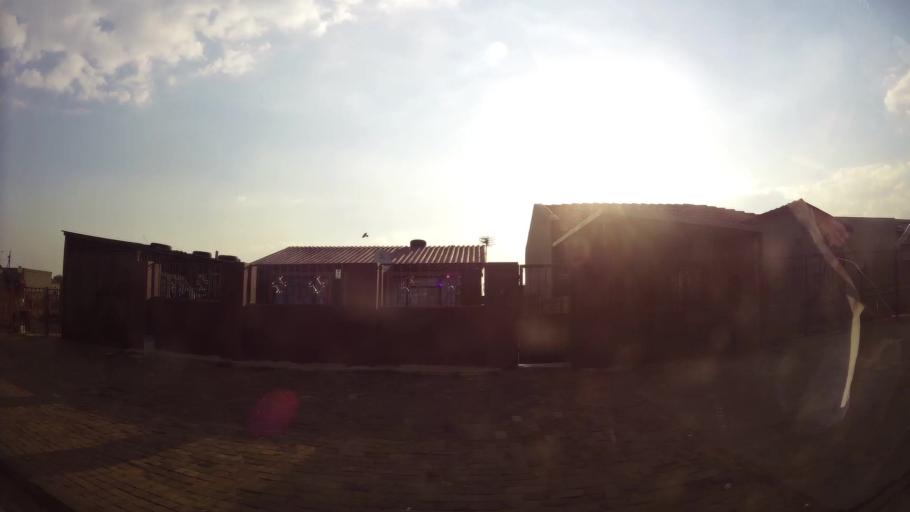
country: ZA
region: Gauteng
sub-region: Ekurhuleni Metropolitan Municipality
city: Germiston
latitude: -26.3486
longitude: 28.2088
